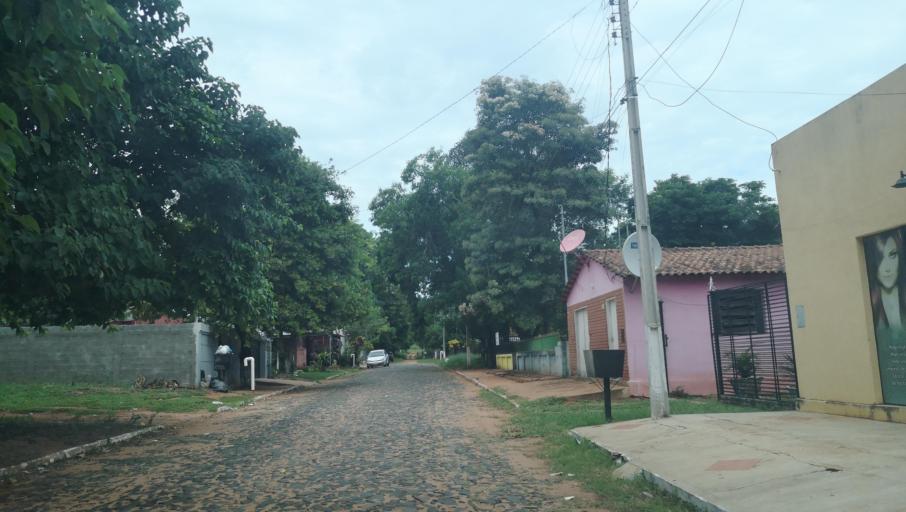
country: PY
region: San Pedro
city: Capiibary
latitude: -24.7292
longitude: -56.0176
